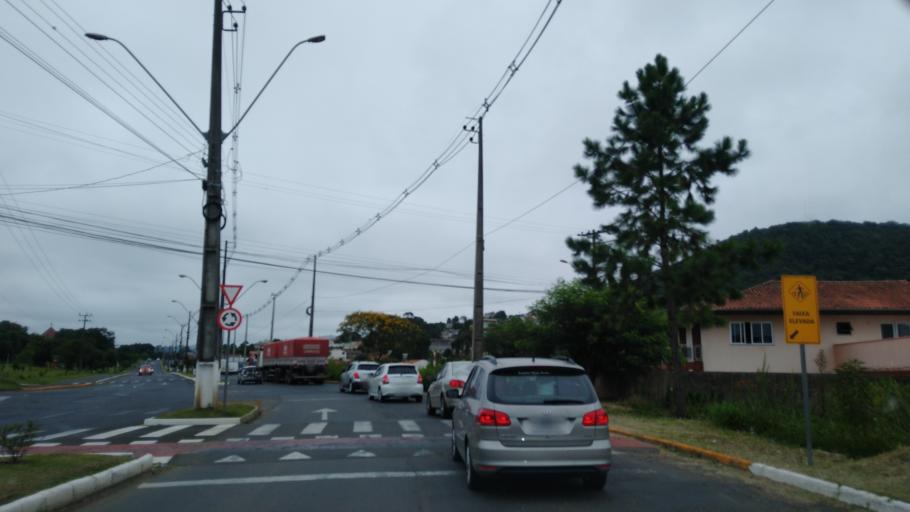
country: BR
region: Santa Catarina
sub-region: Porto Uniao
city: Porto Uniao
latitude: -26.2561
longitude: -51.0745
